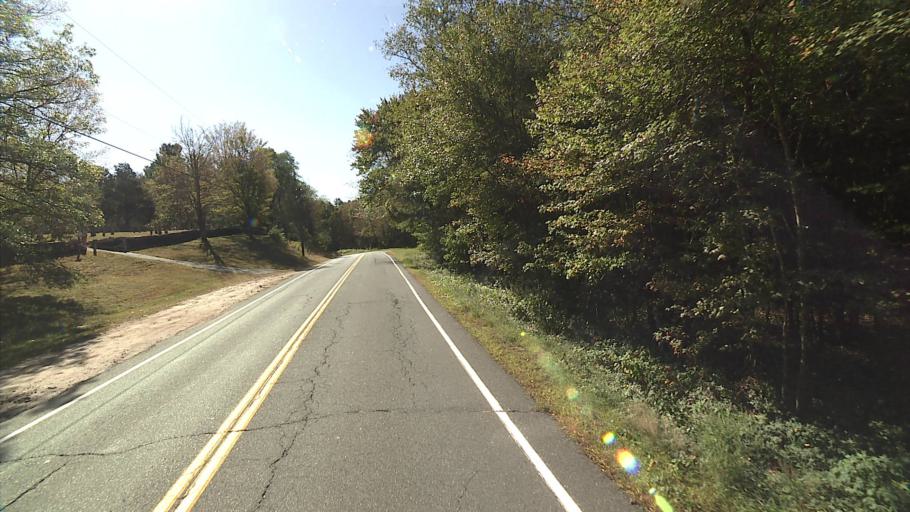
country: US
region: Connecticut
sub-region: Hartford County
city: Bristol
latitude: 41.7435
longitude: -72.9718
